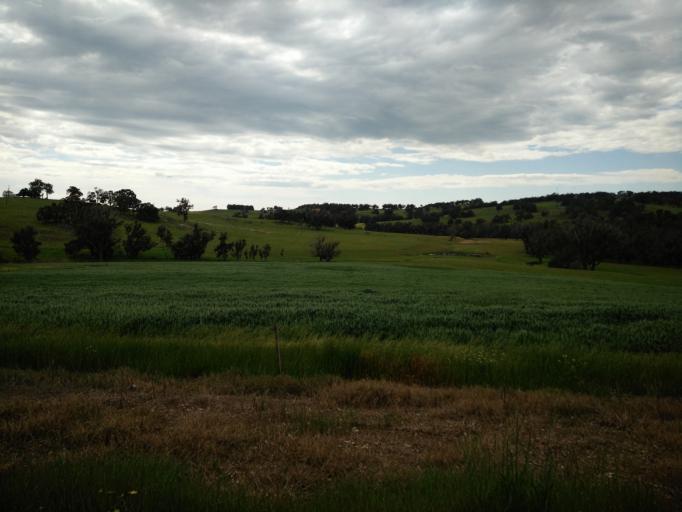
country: AU
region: Western Australia
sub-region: Boyup Brook
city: Boyup Brook
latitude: -33.8494
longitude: 116.3846
